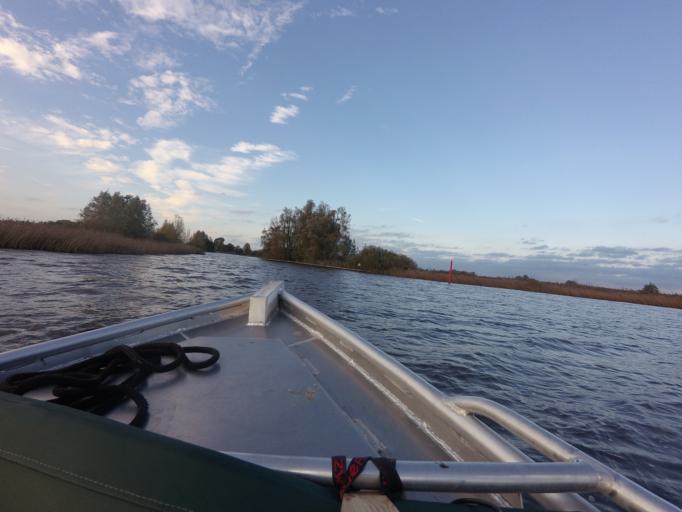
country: NL
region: Overijssel
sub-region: Gemeente Steenwijkerland
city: Blokzijl
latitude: 52.7372
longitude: 5.9949
